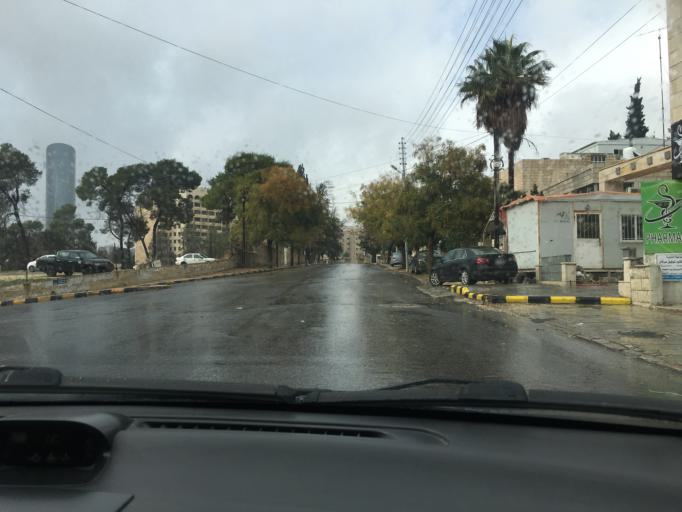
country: JO
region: Amman
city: Amman
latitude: 31.9663
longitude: 35.9133
